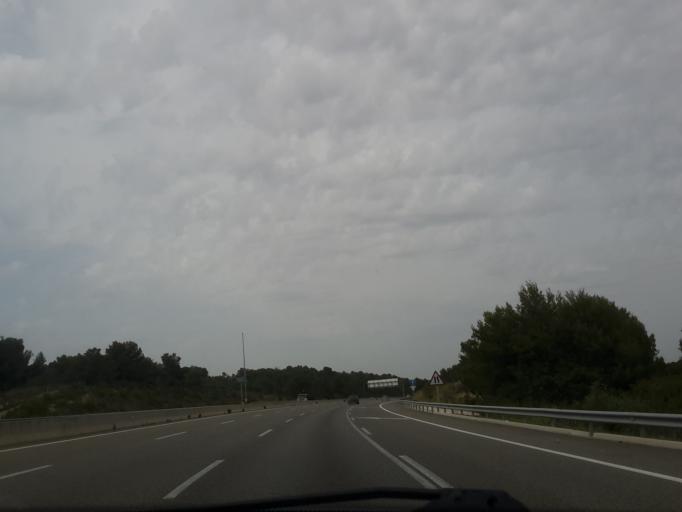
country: ES
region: Catalonia
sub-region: Provincia de Tarragona
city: El Vendrell
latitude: 41.2174
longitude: 1.5144
